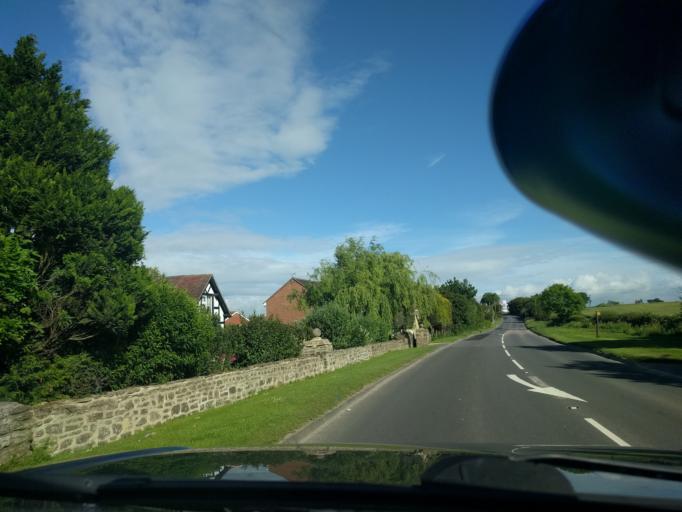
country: GB
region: England
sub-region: Wiltshire
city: Royal Wootton Bassett
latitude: 51.5479
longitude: -1.8875
